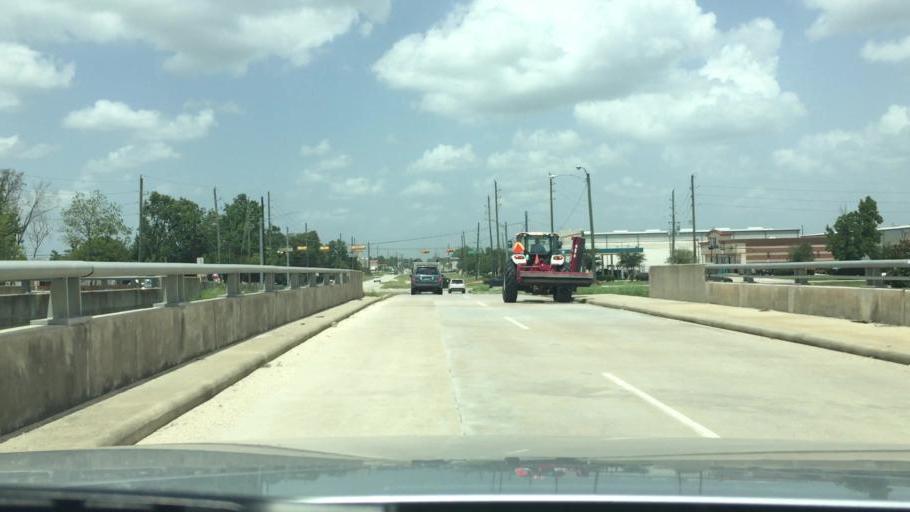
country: US
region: Texas
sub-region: Harris County
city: Hudson
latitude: 29.9493
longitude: -95.5197
